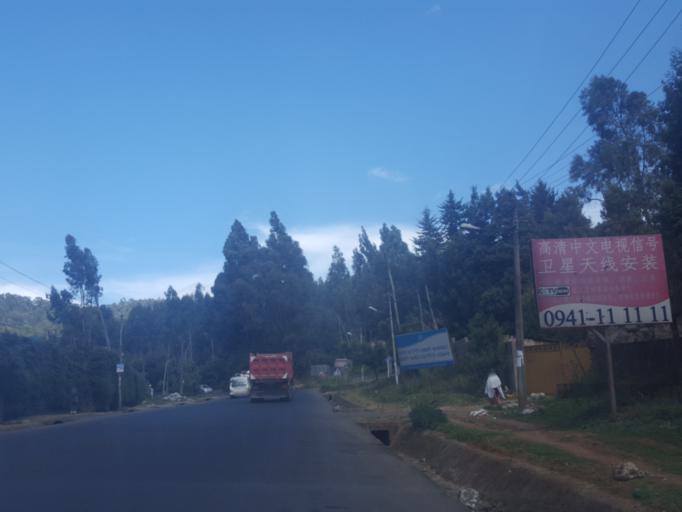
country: ET
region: Adis Abeba
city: Addis Ababa
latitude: 9.0731
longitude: 38.7381
